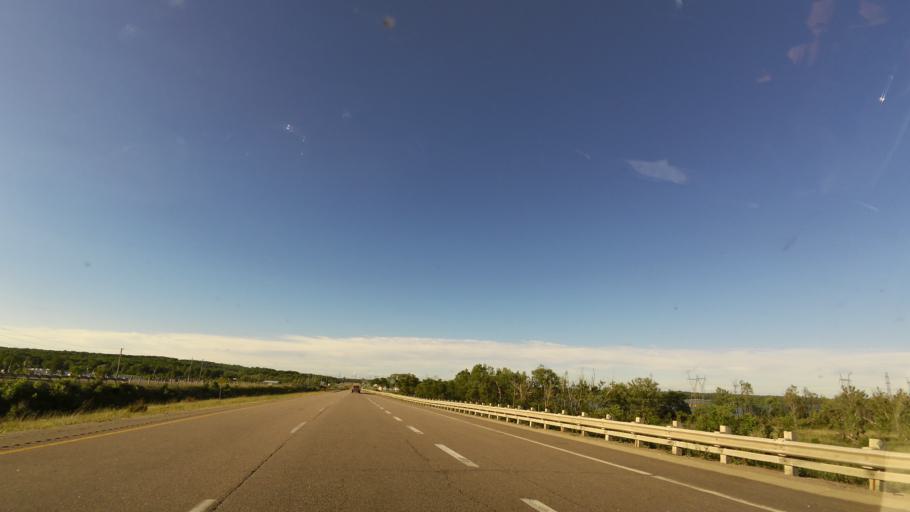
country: CA
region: Ontario
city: Midland
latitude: 44.7537
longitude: -79.7025
